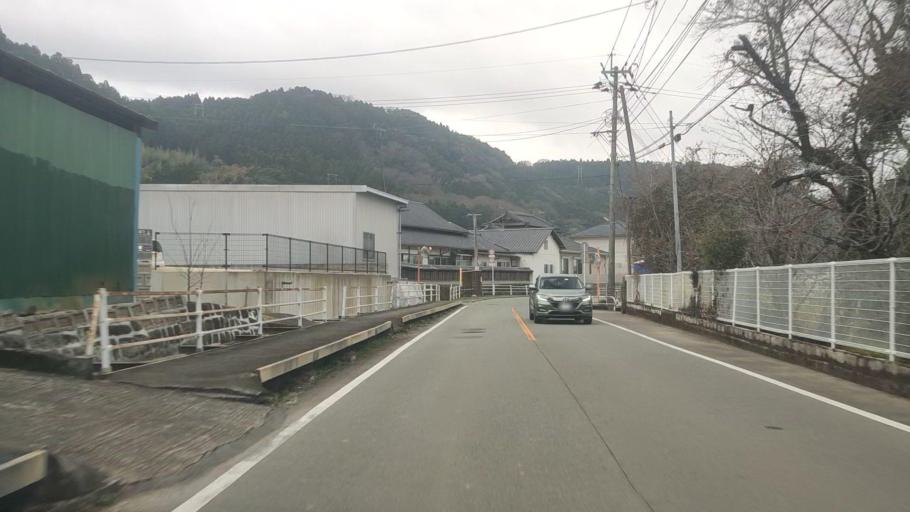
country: JP
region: Kumamoto
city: Ozu
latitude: 32.8553
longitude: 130.8826
